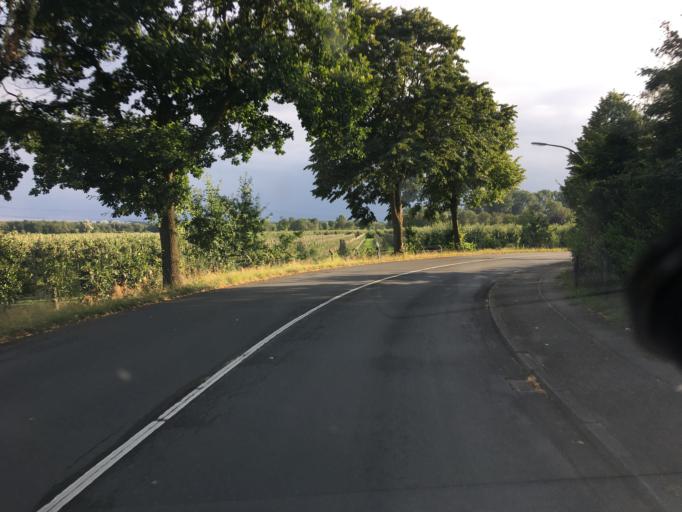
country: DE
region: Hamburg
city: Altona
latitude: 53.4993
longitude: 9.8778
